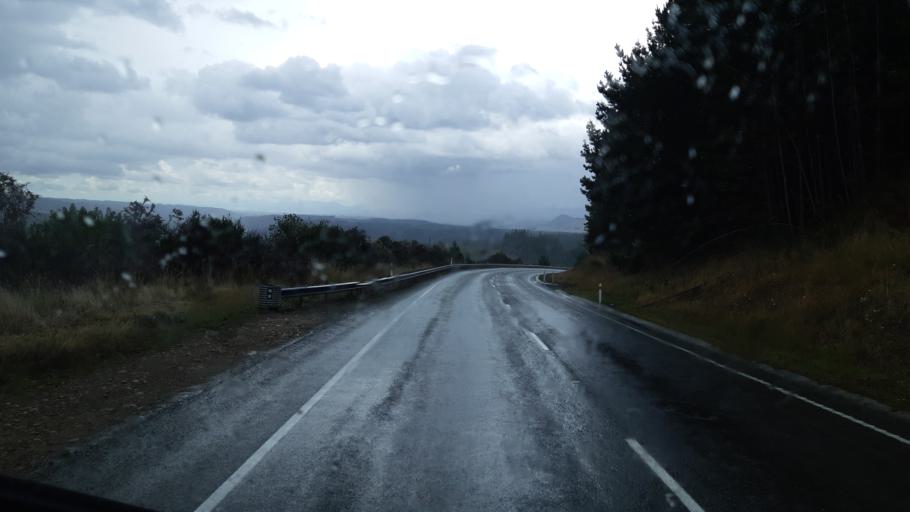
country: NZ
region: Tasman
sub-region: Tasman District
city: Wakefield
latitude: -41.4794
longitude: 172.9187
